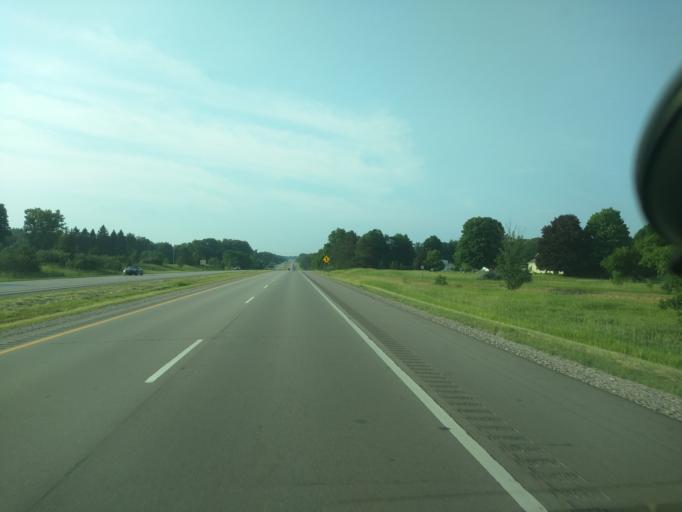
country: US
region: Michigan
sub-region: Ingham County
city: Leslie
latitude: 42.3804
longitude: -84.4289
